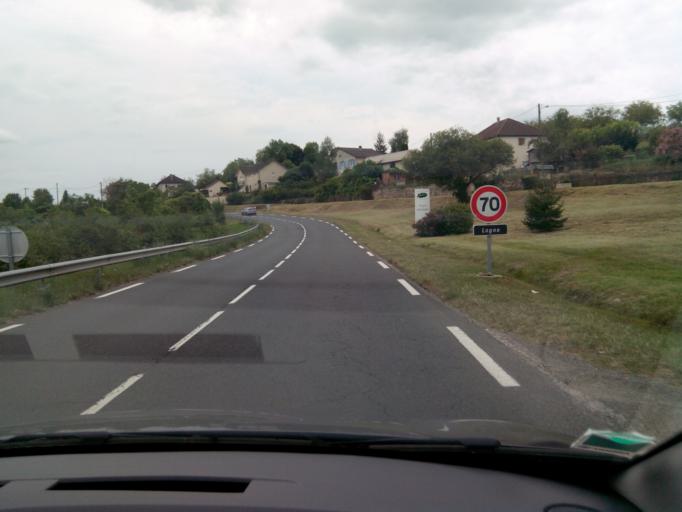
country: FR
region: Limousin
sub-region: Departement de la Correze
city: Cosnac
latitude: 45.0874
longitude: 1.5640
